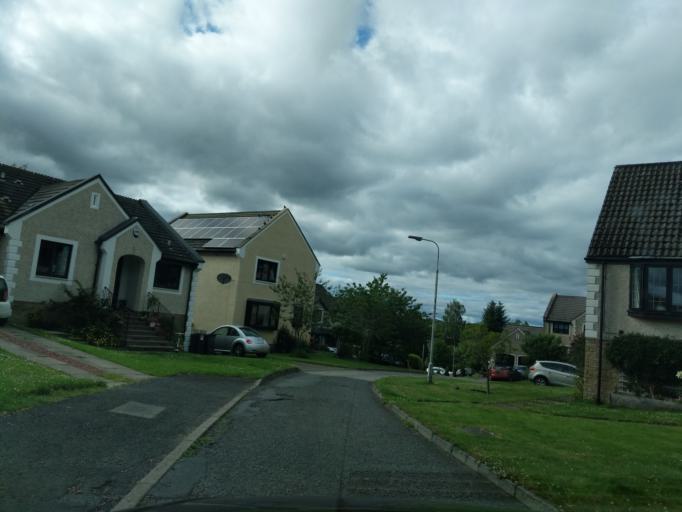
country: GB
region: Scotland
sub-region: The Scottish Borders
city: Peebles
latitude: 55.7138
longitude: -3.2038
